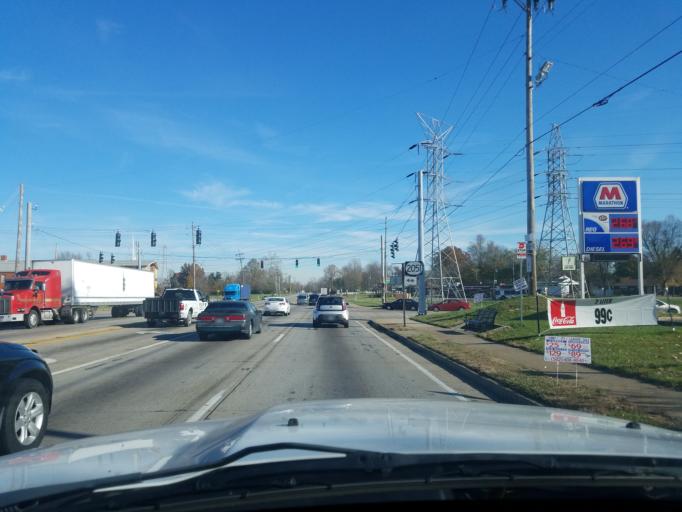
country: US
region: Kentucky
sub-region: Jefferson County
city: Saint Dennis
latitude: 38.1834
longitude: -85.8556
